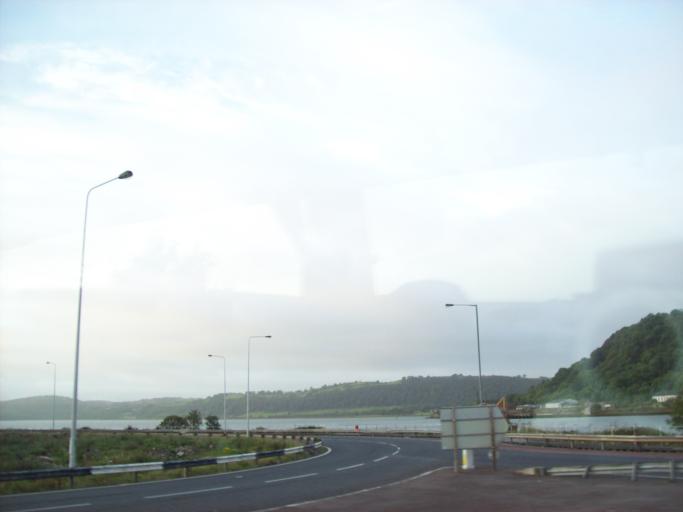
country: GB
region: Northern Ireland
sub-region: Larne District
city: Larne
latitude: 54.8479
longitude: -5.8160
